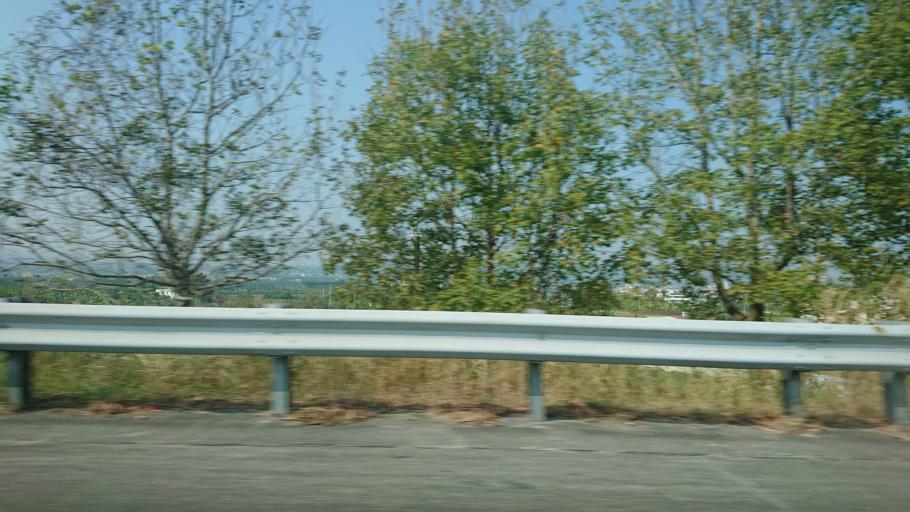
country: TW
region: Taiwan
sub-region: Nantou
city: Nantou
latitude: 23.8869
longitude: 120.7098
